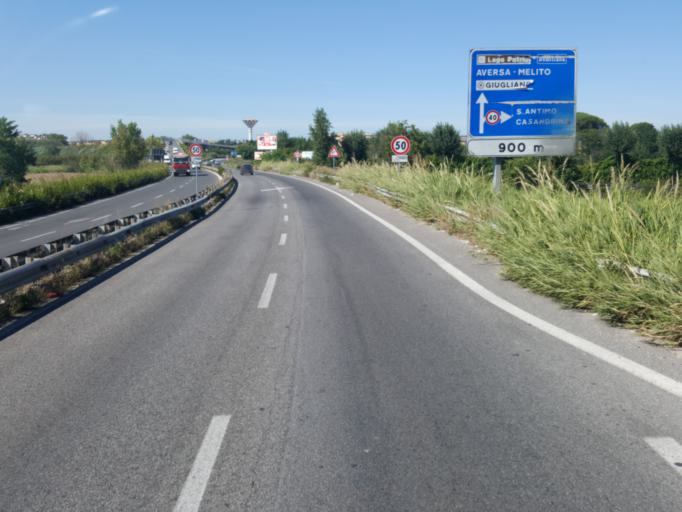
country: IT
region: Campania
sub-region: Provincia di Napoli
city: Casandrino
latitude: 40.9289
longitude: 14.2457
